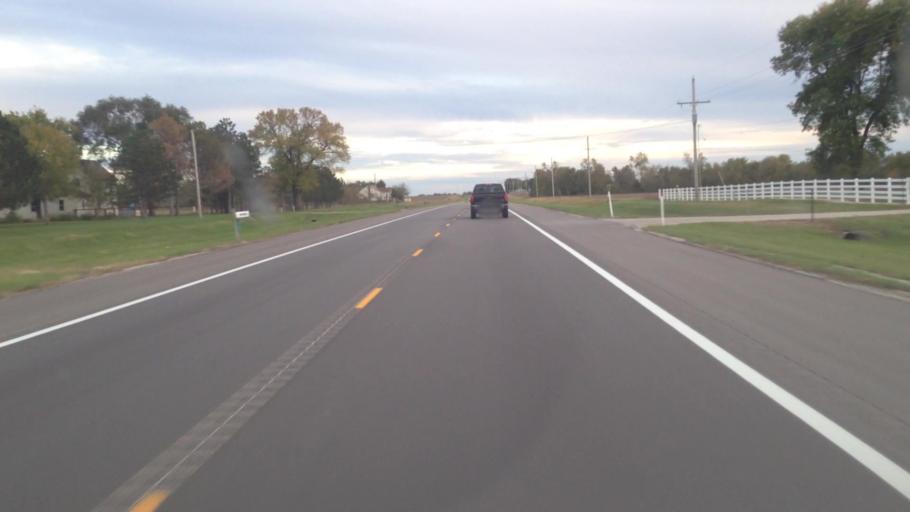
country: US
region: Kansas
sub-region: Franklin County
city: Ottawa
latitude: 38.5432
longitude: -95.2678
